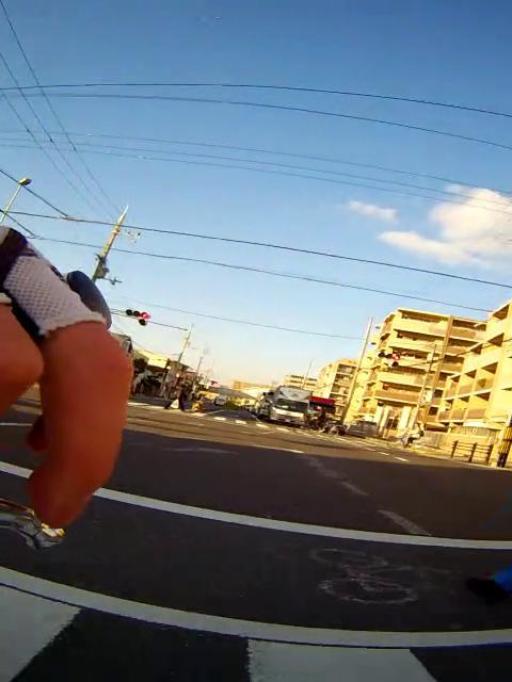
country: JP
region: Hyogo
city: Amagasaki
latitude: 34.7514
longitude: 135.4220
